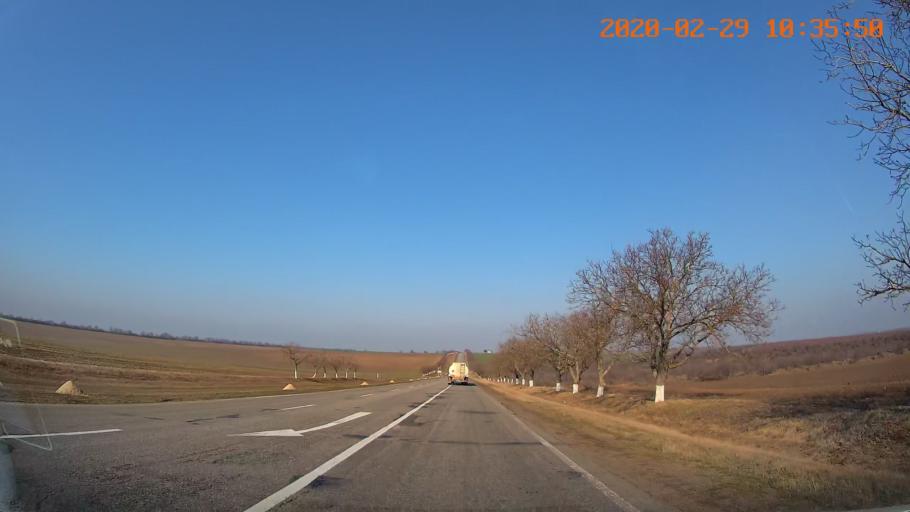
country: MD
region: Anenii Noi
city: Varnita
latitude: 46.9894
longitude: 29.5148
